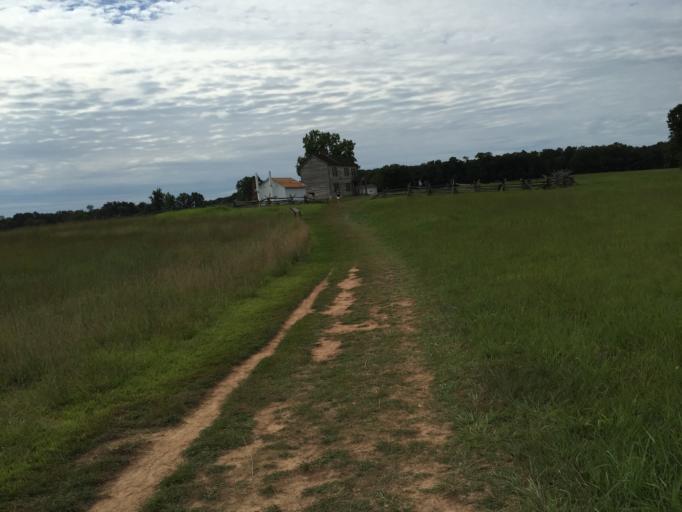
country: US
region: Virginia
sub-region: Prince William County
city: Bull Run
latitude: 38.8157
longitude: -77.5231
